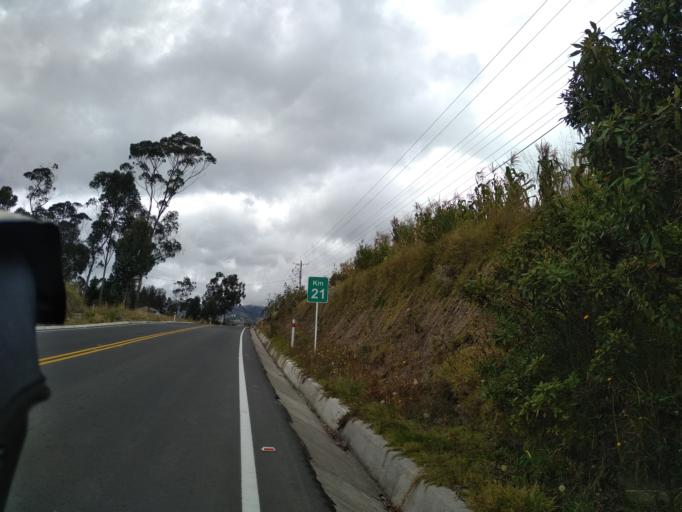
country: EC
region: Cotopaxi
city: Saquisili
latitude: -0.7916
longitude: -78.9127
